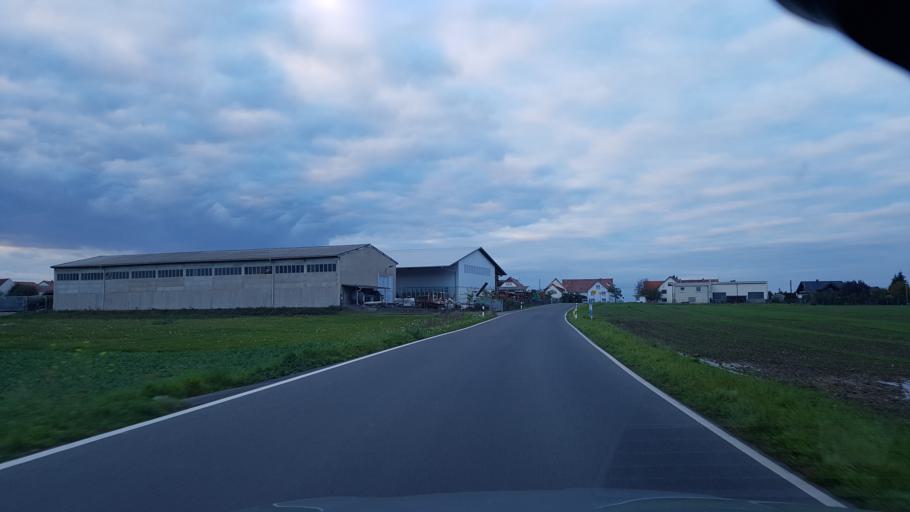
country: DE
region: Saxony
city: Grossenhain
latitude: 51.2670
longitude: 13.5938
